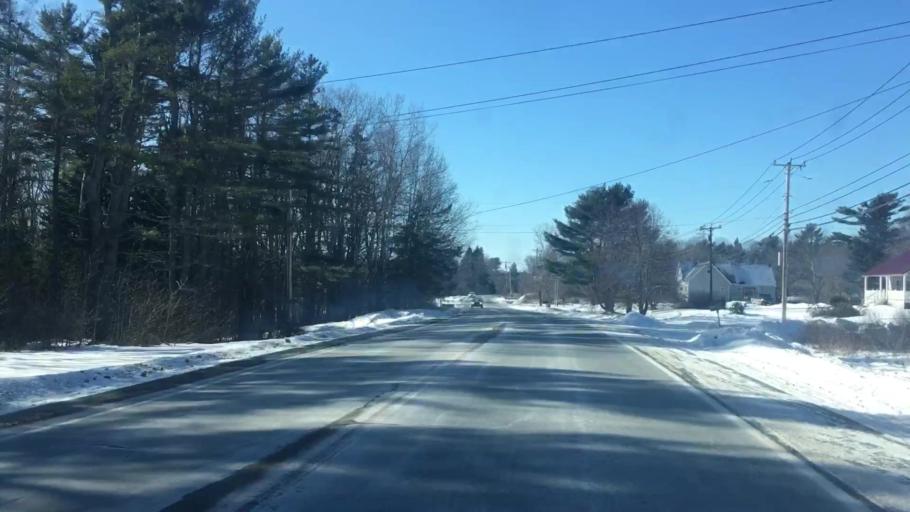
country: US
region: Maine
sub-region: Hancock County
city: Surry
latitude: 44.4970
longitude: -68.4930
